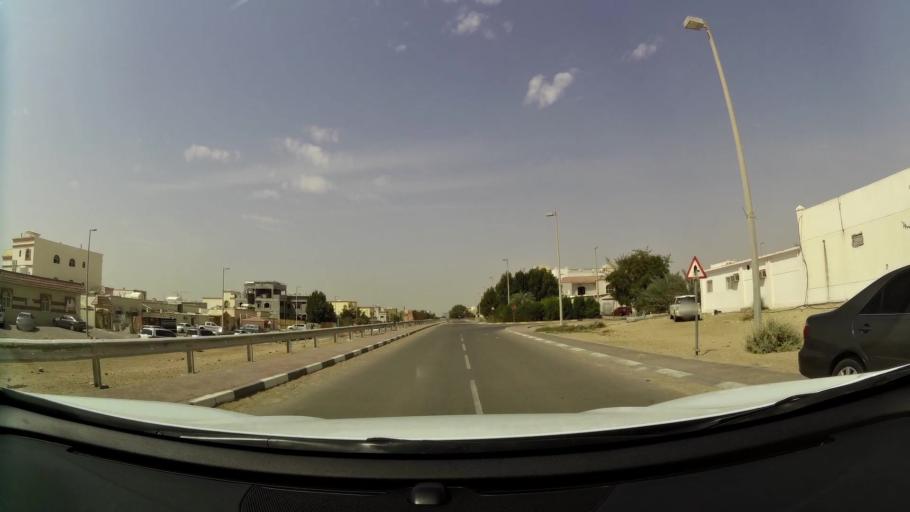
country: AE
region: Abu Dhabi
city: Abu Dhabi
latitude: 24.3001
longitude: 54.6443
